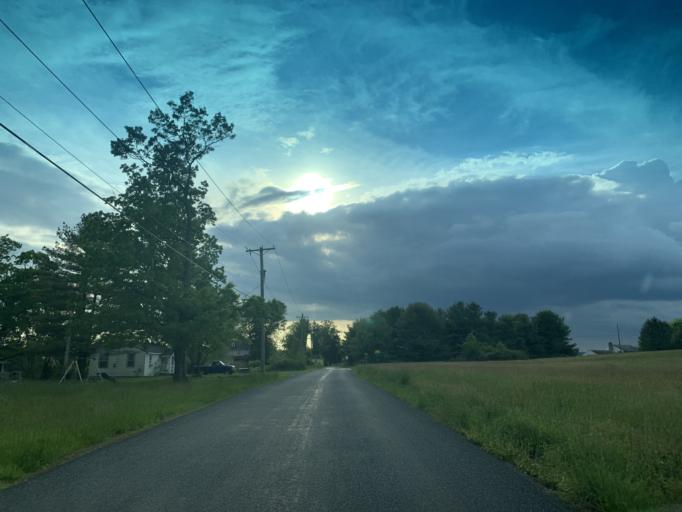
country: US
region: Pennsylvania
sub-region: York County
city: Susquehanna Trails
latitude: 39.6712
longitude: -76.2566
